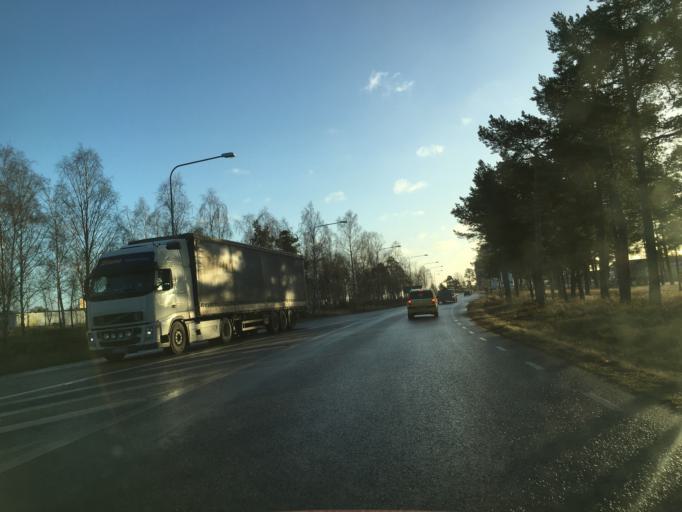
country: SE
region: Kalmar
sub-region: Vasterviks Kommun
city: Vaestervik
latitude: 57.7648
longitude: 16.6006
